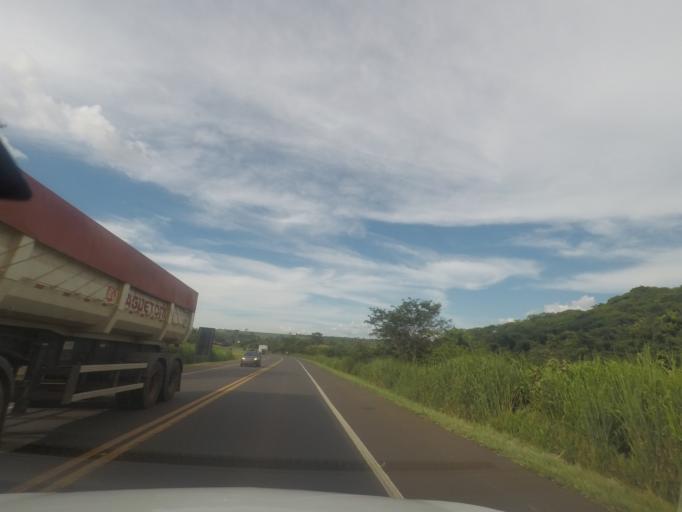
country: BR
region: Minas Gerais
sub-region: Monte Alegre De Minas
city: Monte Alegre de Minas
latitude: -19.0465
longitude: -49.0107
